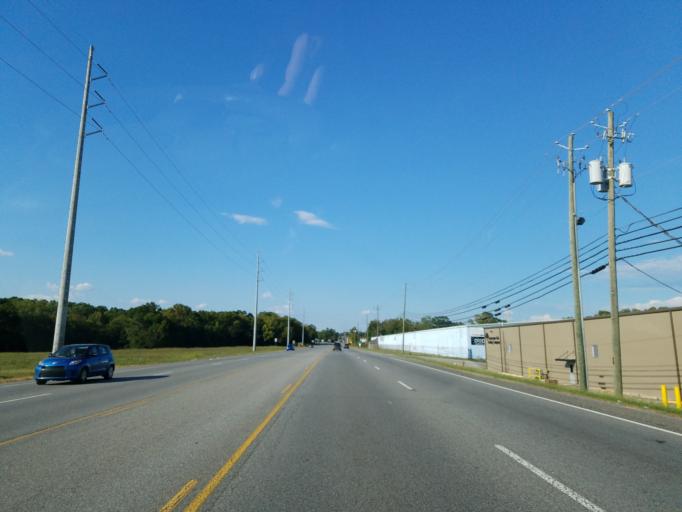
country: US
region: Georgia
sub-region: Murray County
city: Chatsworth
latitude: 34.8149
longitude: -84.7654
